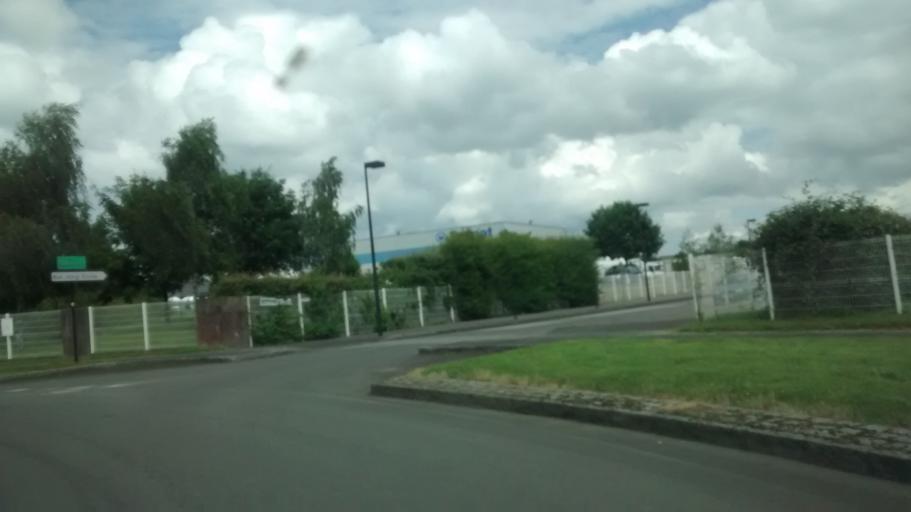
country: FR
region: Brittany
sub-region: Departement d'Ille-et-Vilaine
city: Saint-Jacques-de-la-Lande
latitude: 48.0664
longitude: -1.7028
